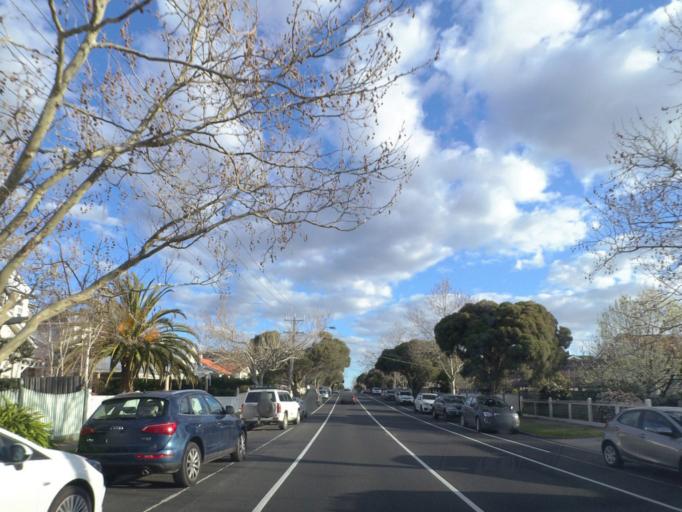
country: AU
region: Victoria
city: Mont Albert
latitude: -37.8166
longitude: 145.0991
